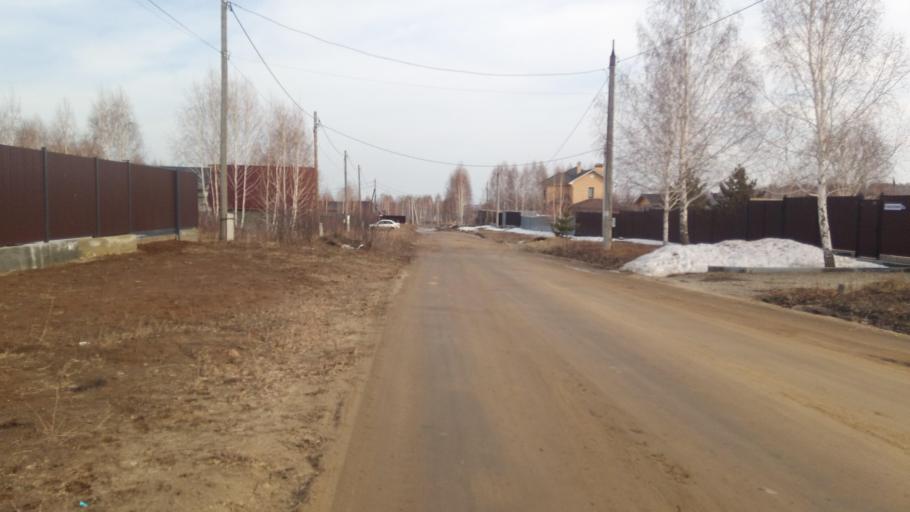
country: RU
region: Chelyabinsk
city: Sargazy
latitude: 55.1043
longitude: 61.2003
